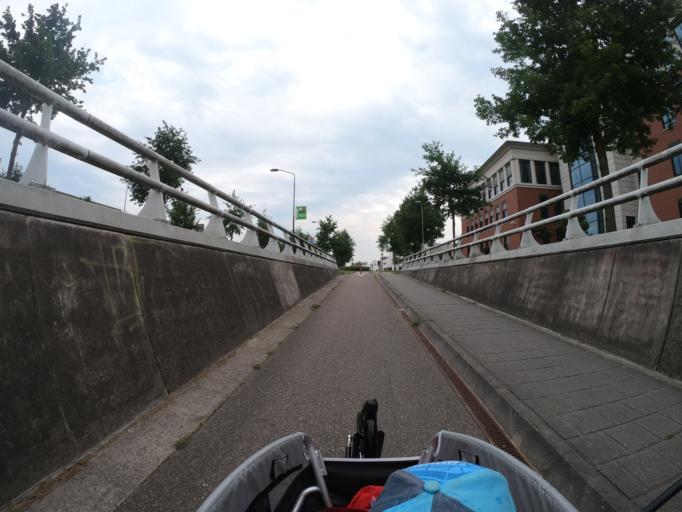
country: NL
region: North Brabant
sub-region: Gemeente Uden
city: Uden
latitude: 51.6479
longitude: 5.6242
